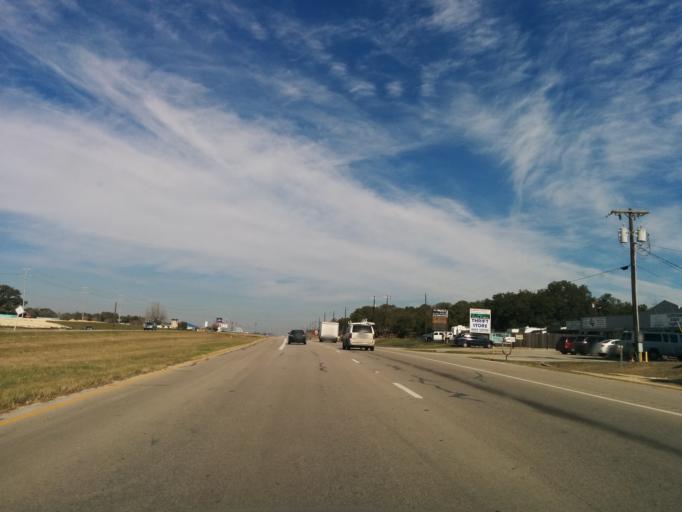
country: US
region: Texas
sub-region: Comal County
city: Bulverde
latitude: 29.8057
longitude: -98.4173
